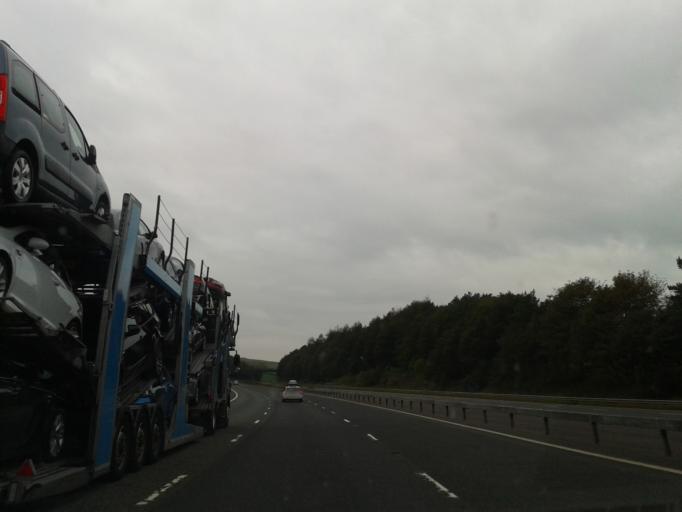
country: GB
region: England
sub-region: Cumbria
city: Sedbergh
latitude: 54.3643
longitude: -2.5986
